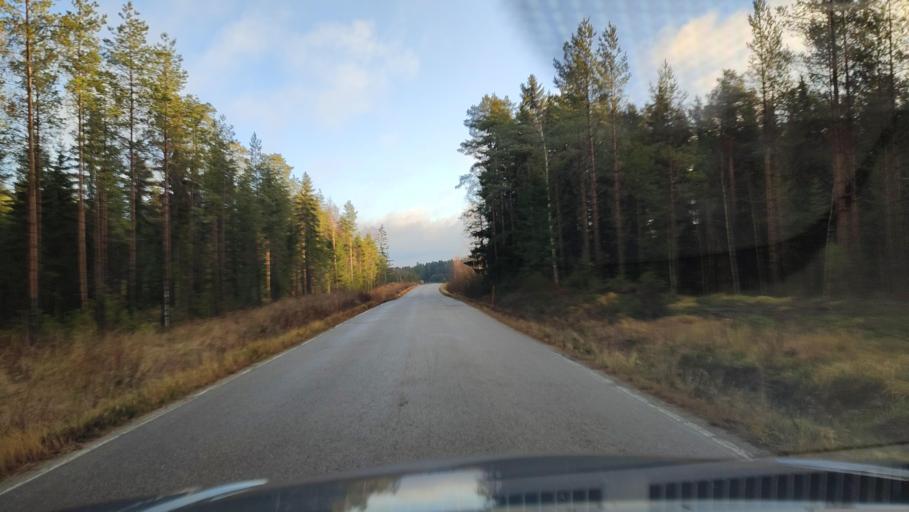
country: FI
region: Ostrobothnia
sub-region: Sydosterbotten
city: Naerpes
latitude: 62.4428
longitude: 21.3944
